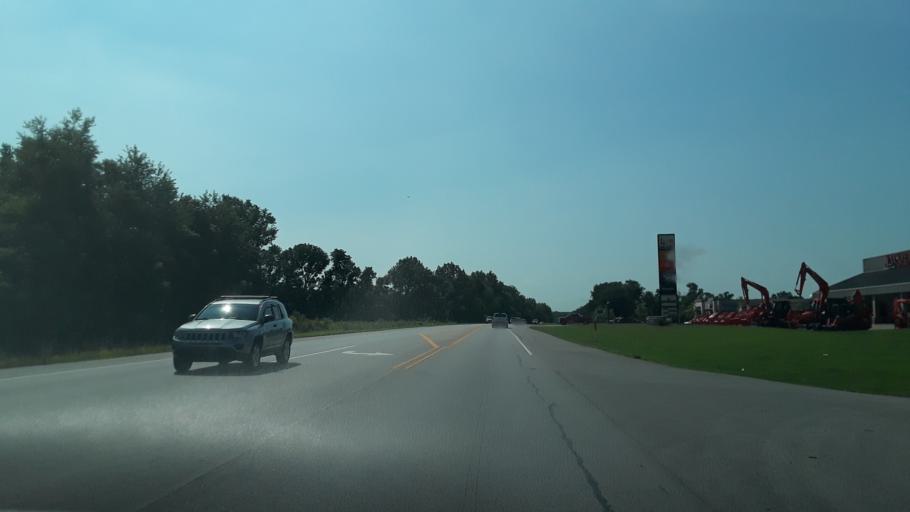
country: US
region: Indiana
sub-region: Clark County
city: Sellersburg
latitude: 38.3793
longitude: -85.7673
